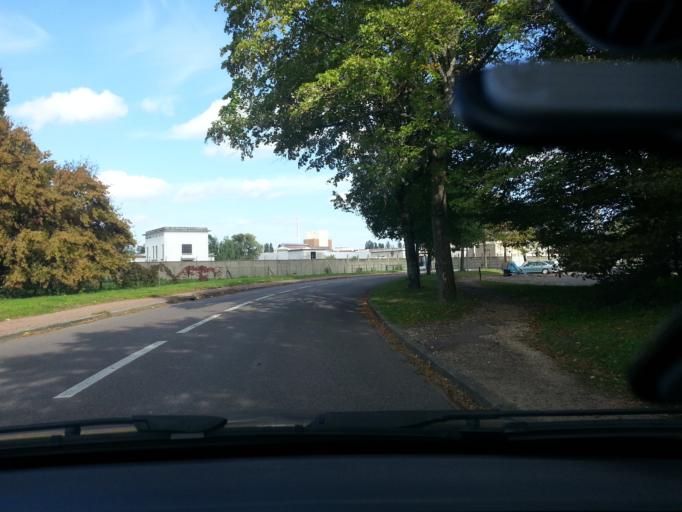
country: FR
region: Bourgogne
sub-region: Departement de Saone-et-Loire
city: Chalon-sur-Saone
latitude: 46.8064
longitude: 4.8549
